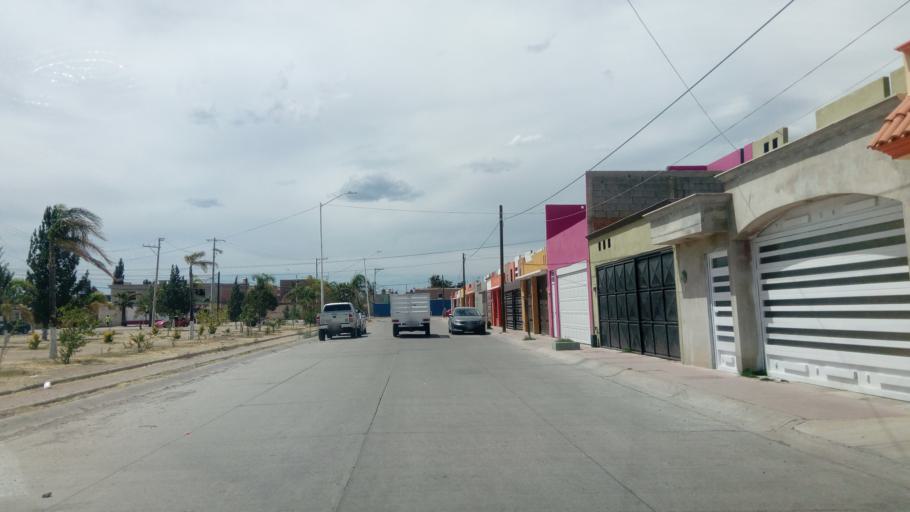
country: MX
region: Durango
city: Victoria de Durango
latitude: 23.9911
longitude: -104.6449
